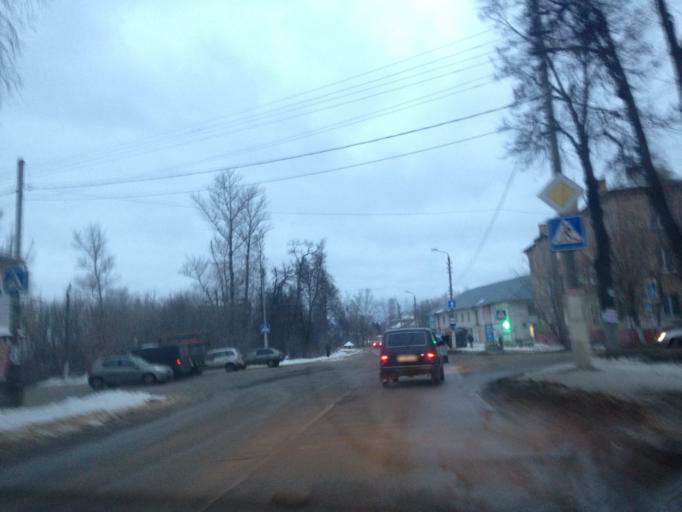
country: RU
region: Tula
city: Shchekino
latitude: 53.9983
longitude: 37.5183
